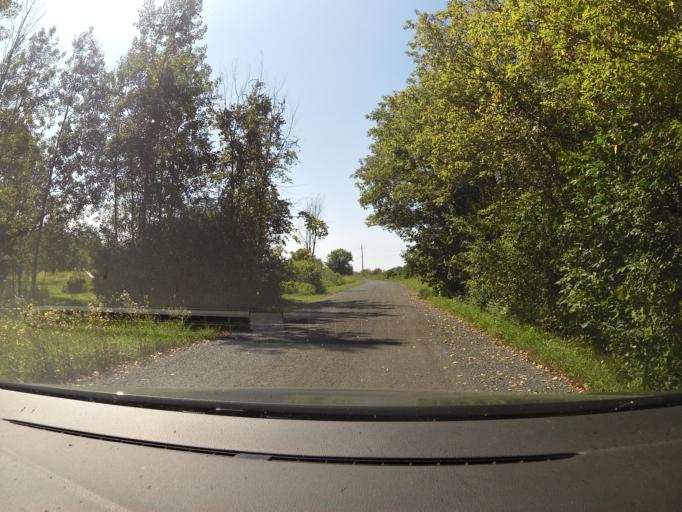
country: CA
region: Ontario
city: Bells Corners
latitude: 45.2888
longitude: -75.9957
